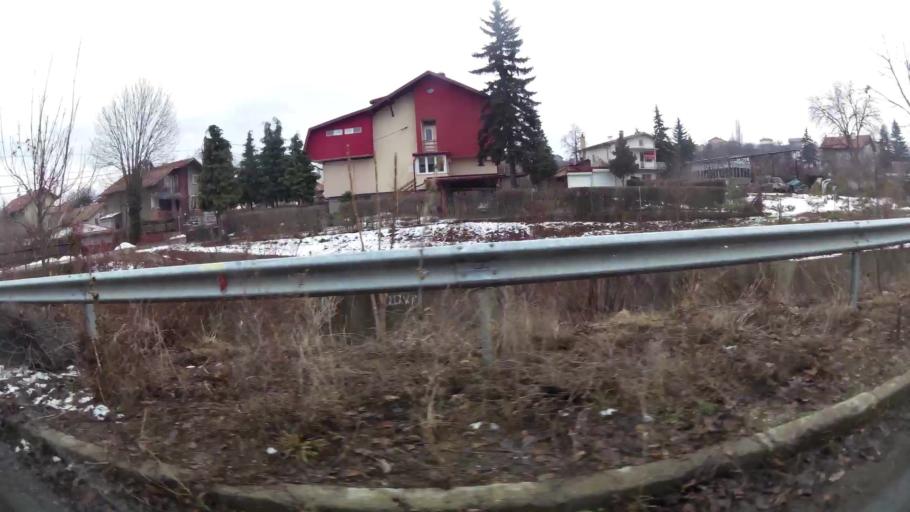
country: BG
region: Sofiya
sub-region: Obshtina Bozhurishte
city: Bozhurishte
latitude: 42.6983
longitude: 23.2228
